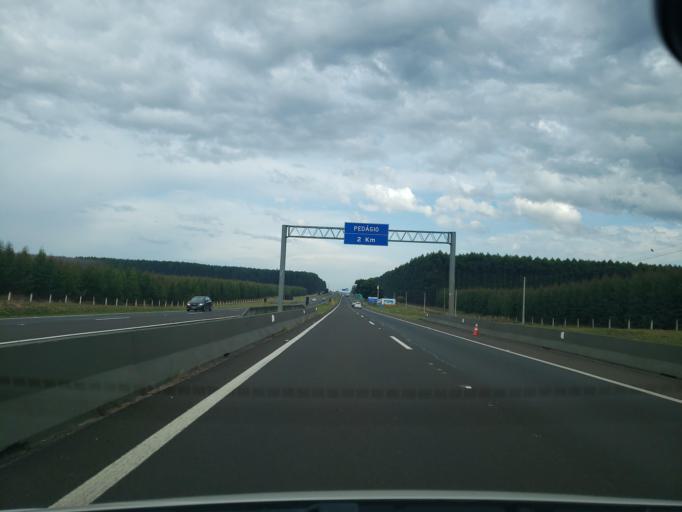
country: BR
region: Sao Paulo
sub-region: Itirapina
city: Itirapina
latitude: -22.2607
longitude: -47.8824
